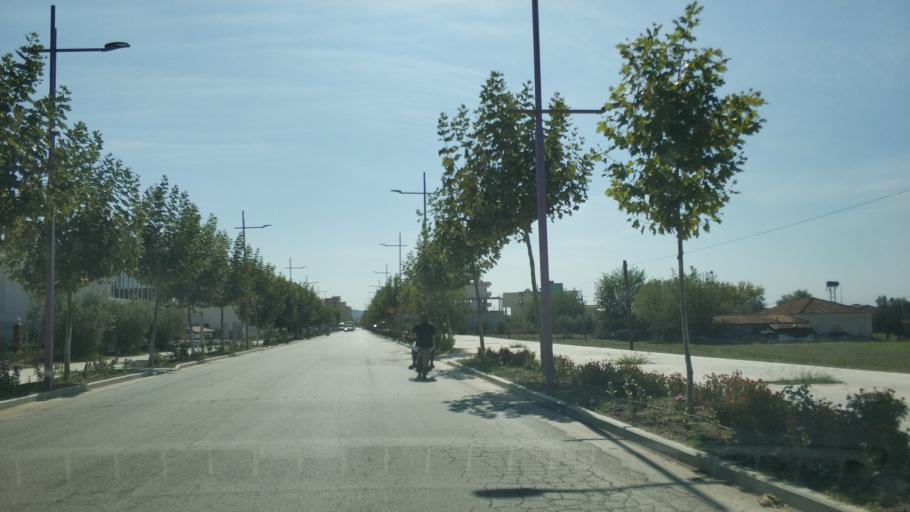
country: AL
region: Fier
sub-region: Rrethi i Lushnjes
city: Divjake
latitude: 41.0041
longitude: 19.5295
